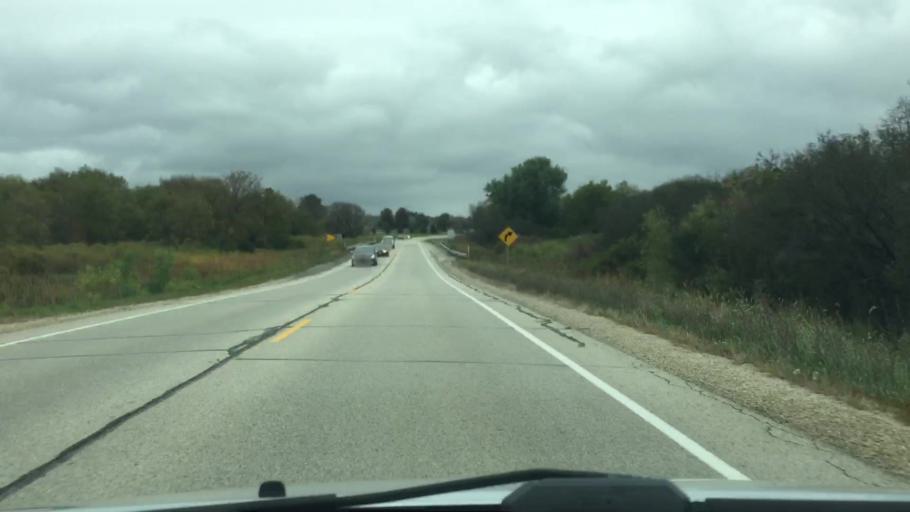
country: US
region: Wisconsin
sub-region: Walworth County
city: Elkhorn
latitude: 42.7357
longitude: -88.5465
